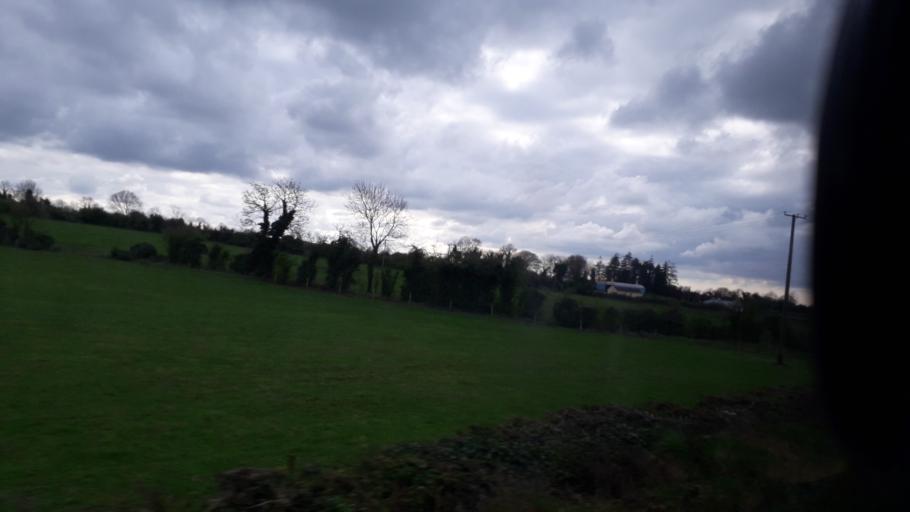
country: IE
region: Leinster
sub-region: An Longfort
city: Edgeworthstown
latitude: 53.7015
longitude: -7.6720
